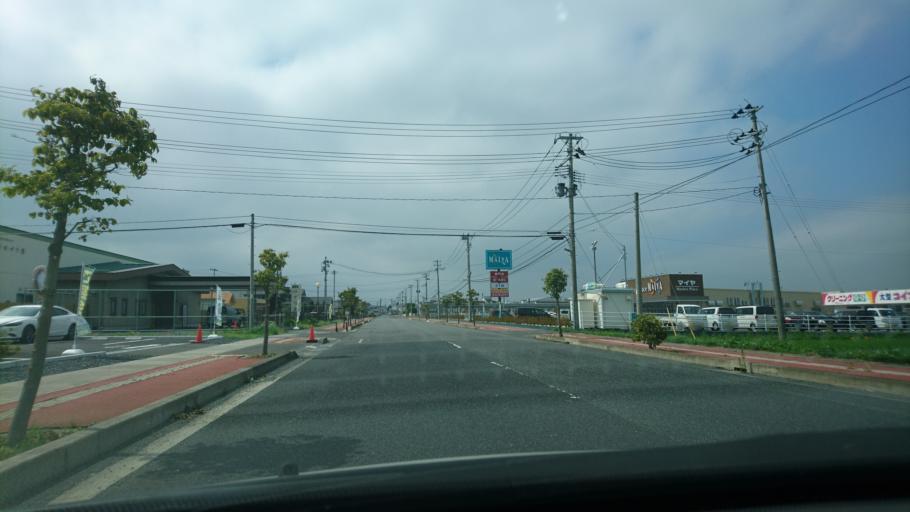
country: JP
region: Iwate
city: Ichinoseki
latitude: 38.8289
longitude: 141.1866
